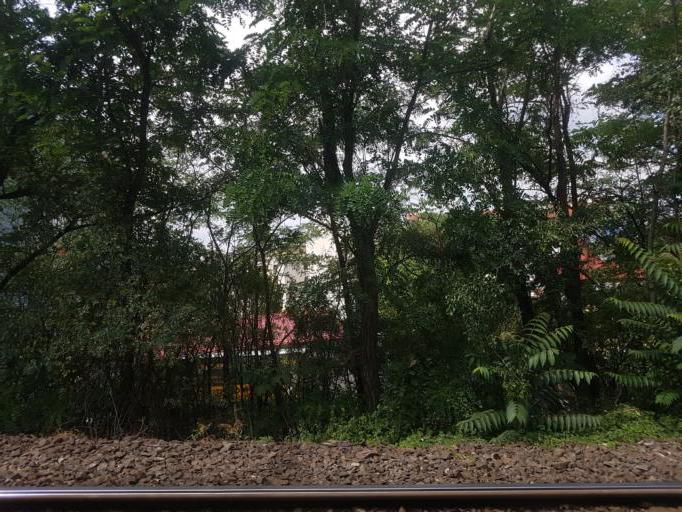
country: CZ
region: Praha
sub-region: Praha 8
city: Liben
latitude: 50.0997
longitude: 14.4732
